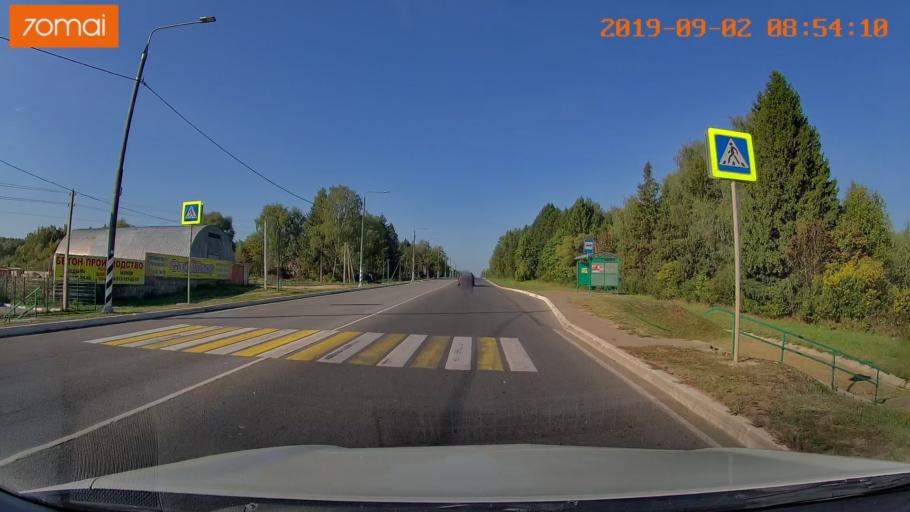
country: RU
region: Kaluga
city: Medyn'
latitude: 54.9633
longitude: 35.8442
